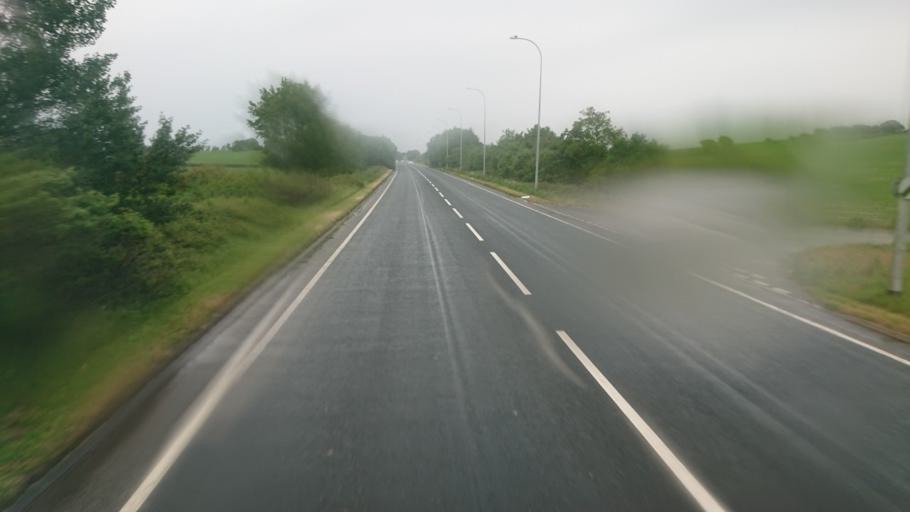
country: GB
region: England
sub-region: Lancashire
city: Morecambe
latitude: 54.0376
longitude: -2.8680
